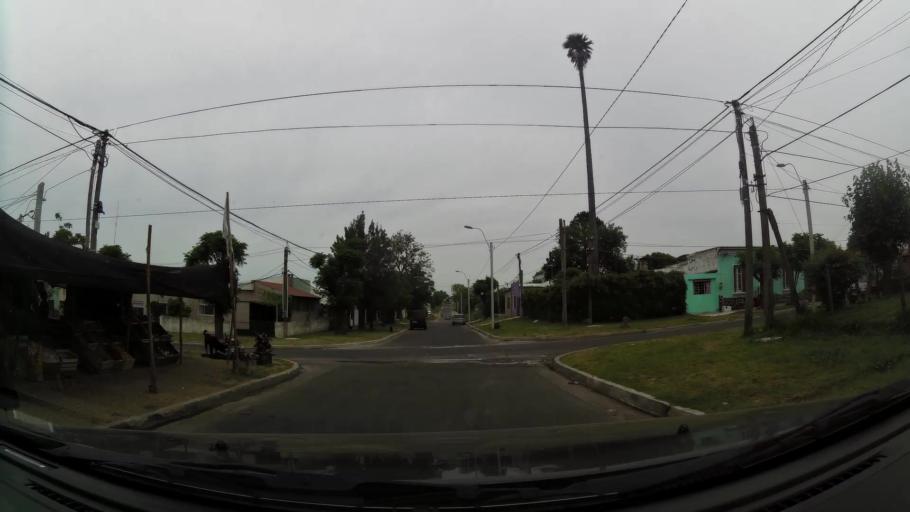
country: UY
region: Canelones
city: Las Piedras
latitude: -34.7294
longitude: -56.2104
